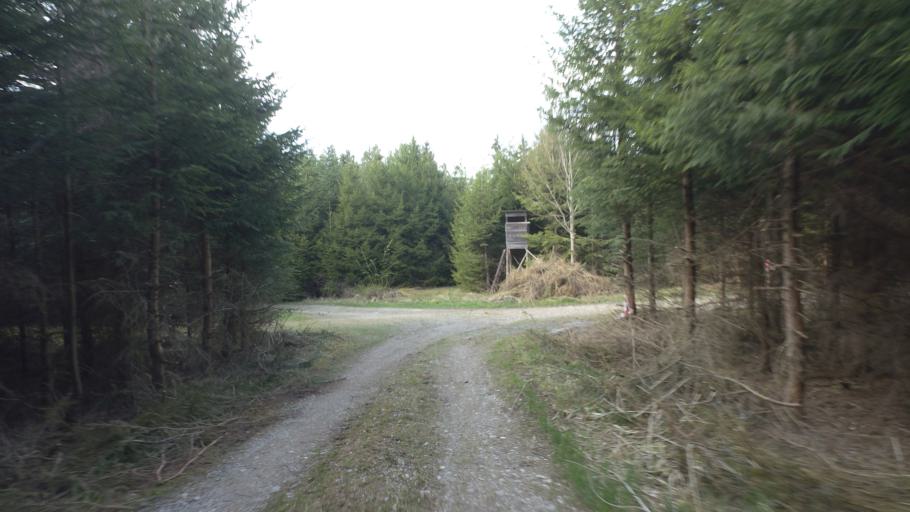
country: DE
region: Bavaria
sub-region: Upper Bavaria
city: Nussdorf
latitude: 47.8962
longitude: 12.5840
